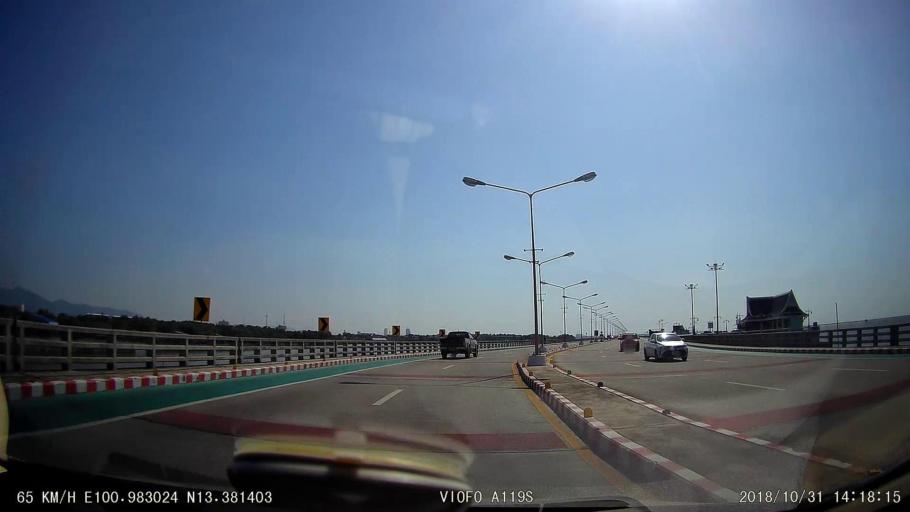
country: TH
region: Chon Buri
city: Chon Buri
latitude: 13.3812
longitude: 100.9829
